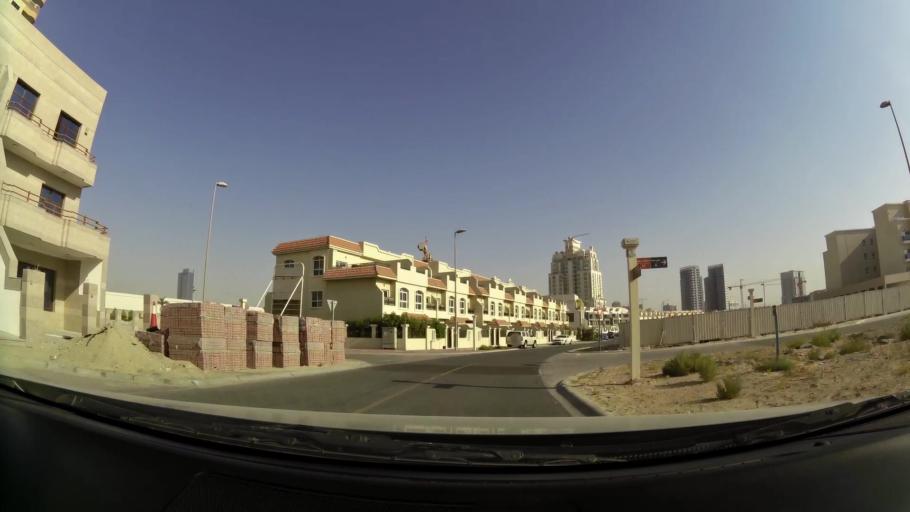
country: AE
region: Dubai
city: Dubai
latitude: 25.0562
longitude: 55.2198
